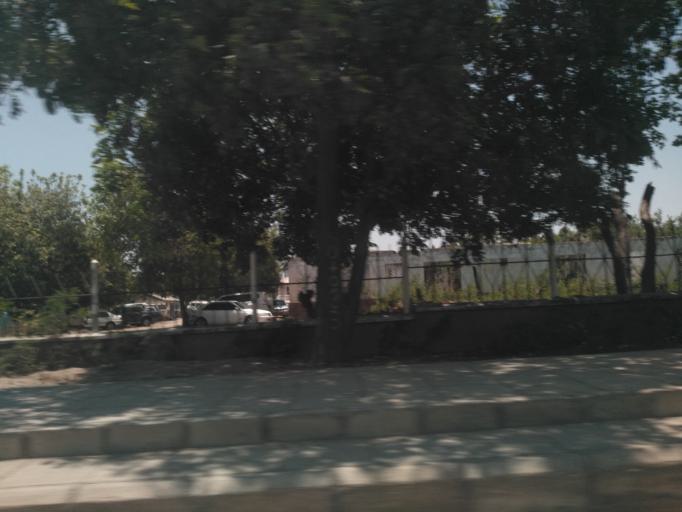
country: TZ
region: Dodoma
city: Dodoma
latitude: -6.1736
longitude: 35.7474
